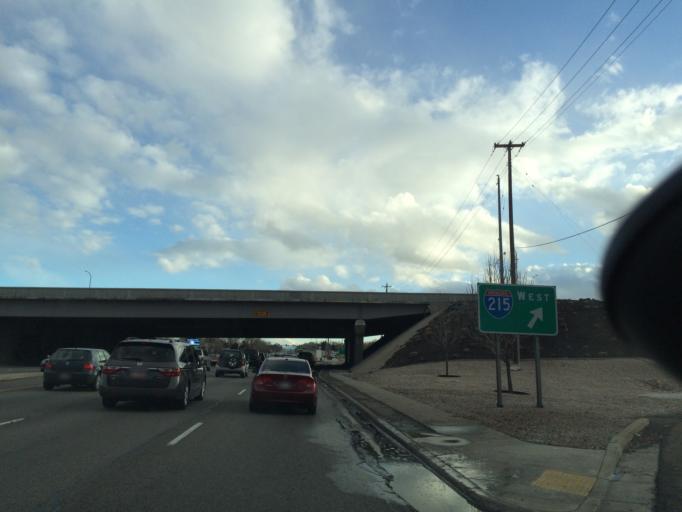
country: US
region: Utah
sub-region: Salt Lake County
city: Taylorsville
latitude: 40.6456
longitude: -111.9389
